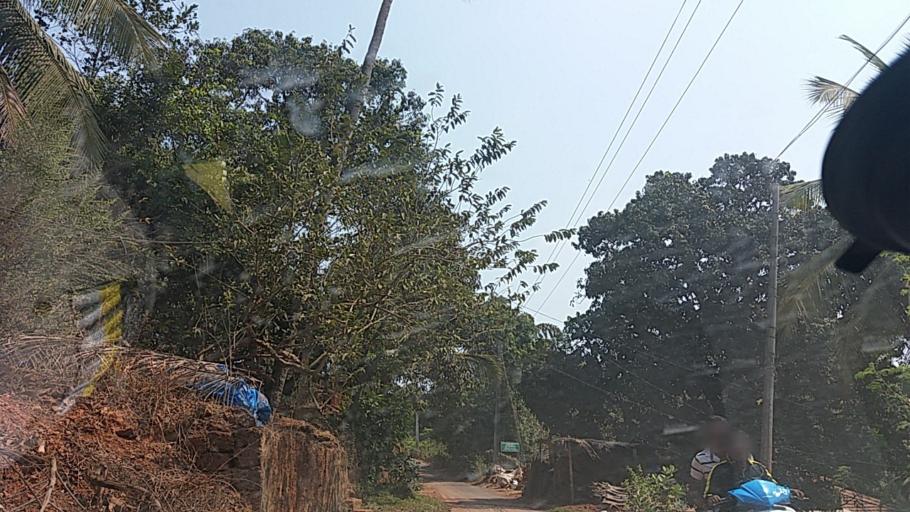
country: IN
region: Goa
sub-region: South Goa
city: Sancoale
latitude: 15.3670
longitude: 73.9154
